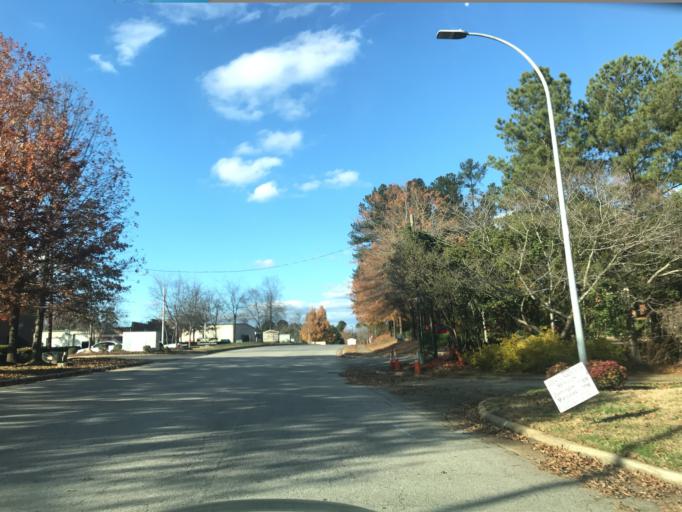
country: US
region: North Carolina
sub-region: Wake County
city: Raleigh
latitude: 35.8524
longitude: -78.5922
